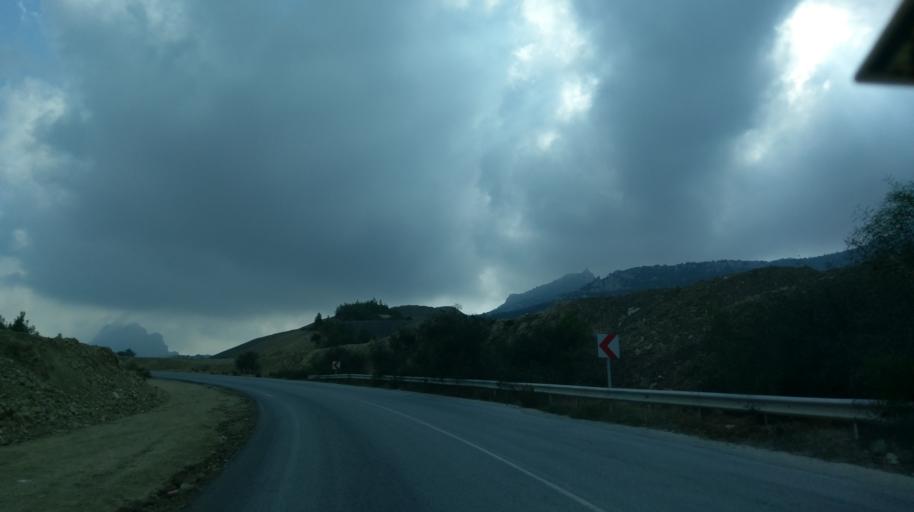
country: CY
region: Keryneia
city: Kyrenia
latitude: 35.2991
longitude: 33.4325
